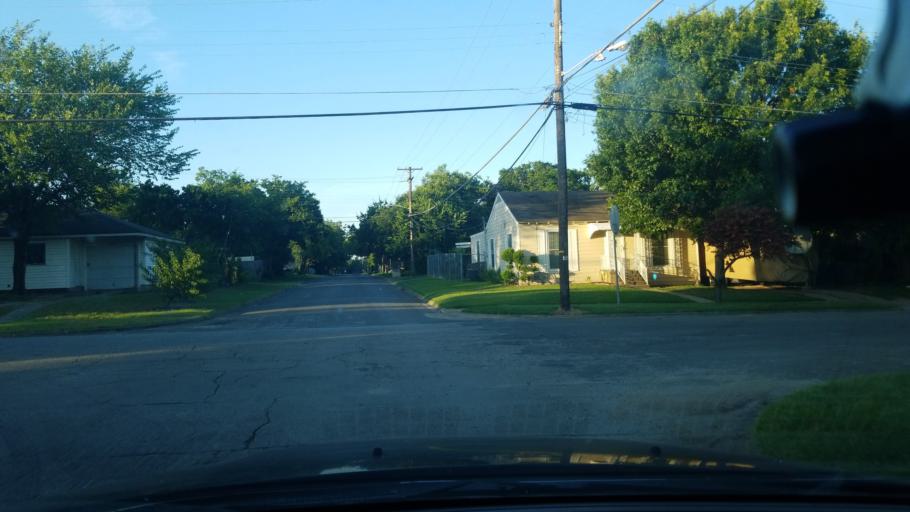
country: US
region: Texas
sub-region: Dallas County
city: Cockrell Hill
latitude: 32.7170
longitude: -96.8265
